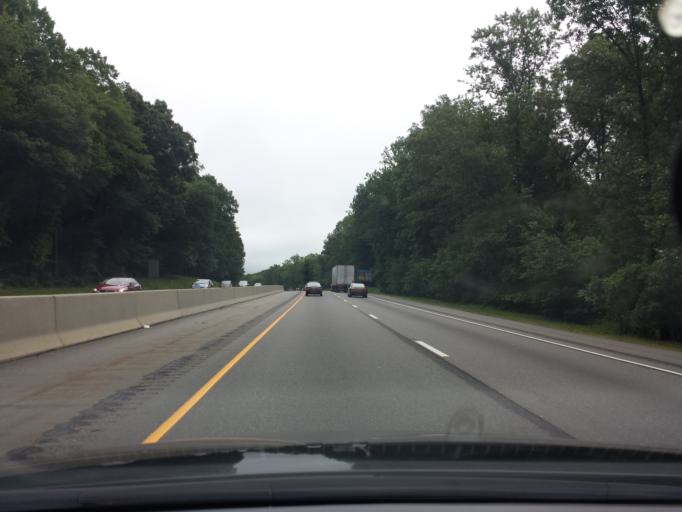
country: US
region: Connecticut
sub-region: Middlesex County
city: Westbrook Center
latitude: 41.2917
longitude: -72.4717
